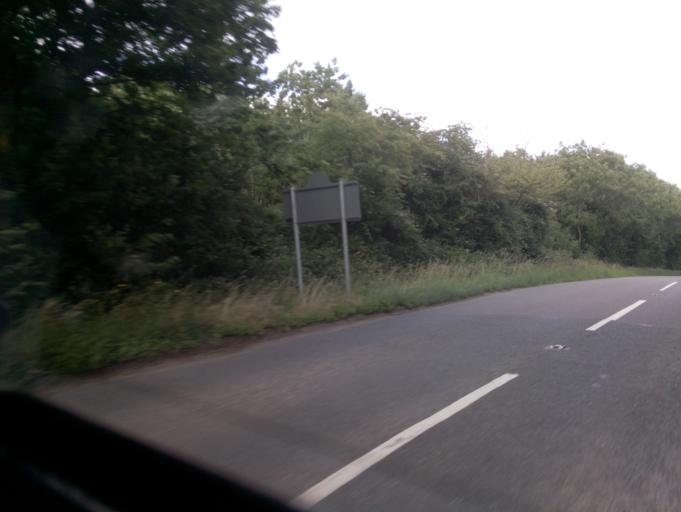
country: GB
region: England
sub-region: Warwickshire
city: Shipston on Stour
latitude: 52.0547
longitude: -1.6900
